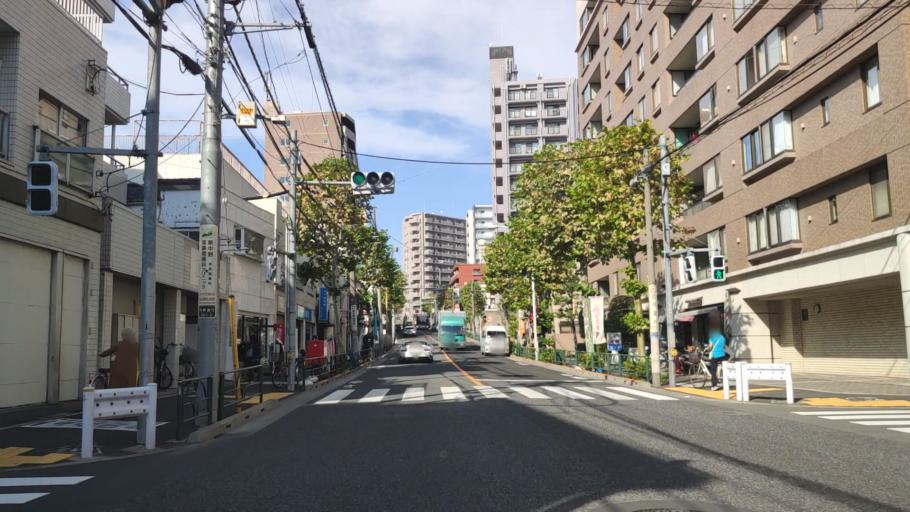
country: JP
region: Tokyo
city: Tokyo
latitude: 35.6923
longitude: 139.6689
